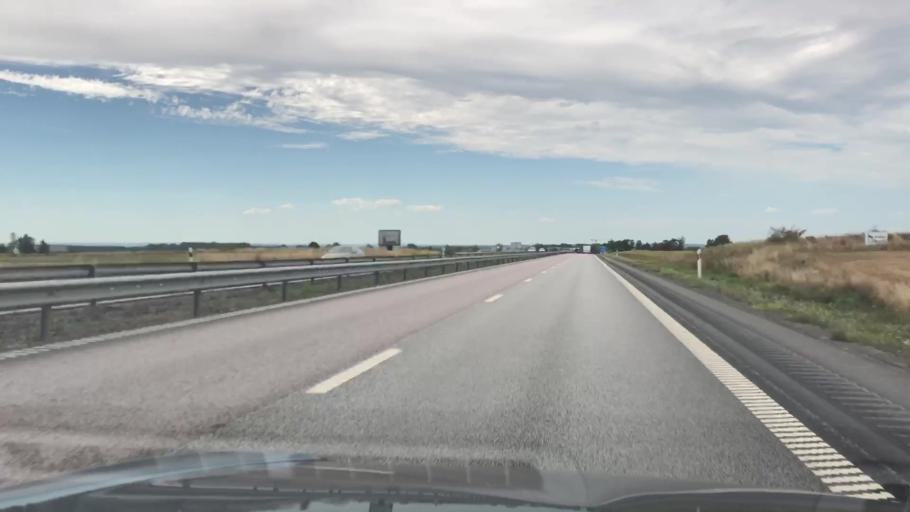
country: SE
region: Skane
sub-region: Kristianstads Kommun
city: Fjalkinge
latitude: 56.0314
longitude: 14.2379
